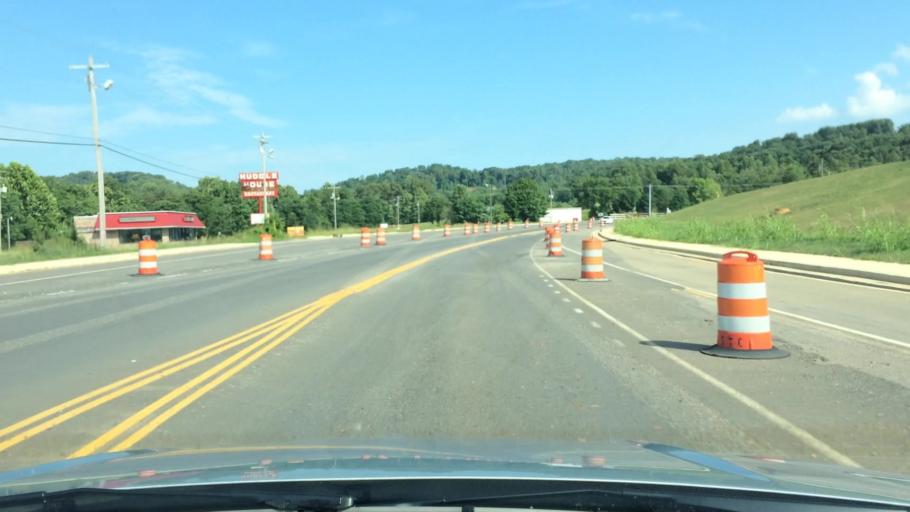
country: US
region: Tennessee
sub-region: Jefferson County
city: White Pine
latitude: 36.1109
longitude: -83.3404
